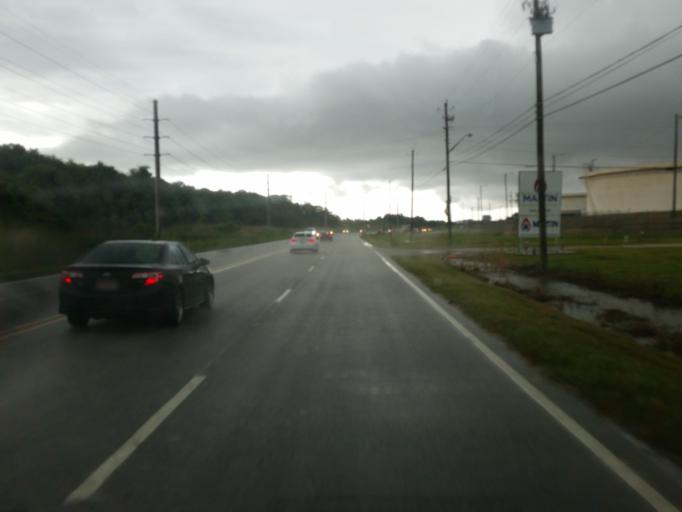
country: US
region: Alabama
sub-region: Mobile County
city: Mobile
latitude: 30.7176
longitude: -88.0348
